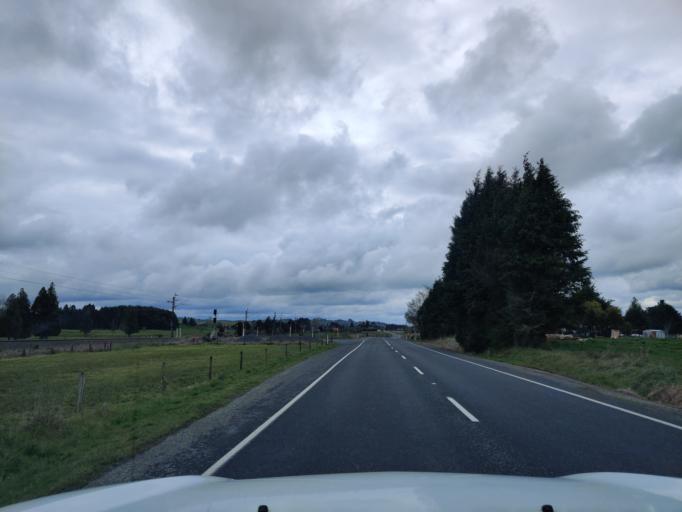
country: NZ
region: Waikato
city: Turangi
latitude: -39.0145
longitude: 175.3783
